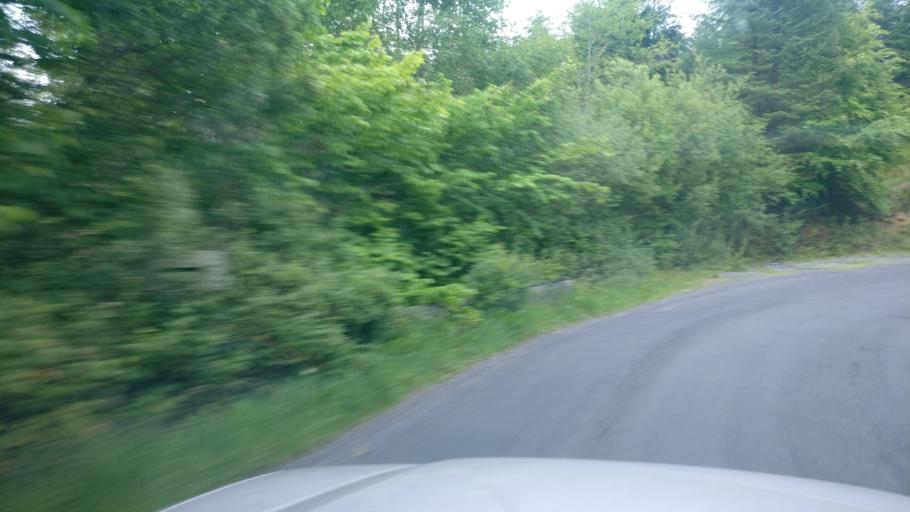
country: IE
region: Connaught
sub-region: County Galway
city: Gort
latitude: 53.0572
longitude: -8.6606
